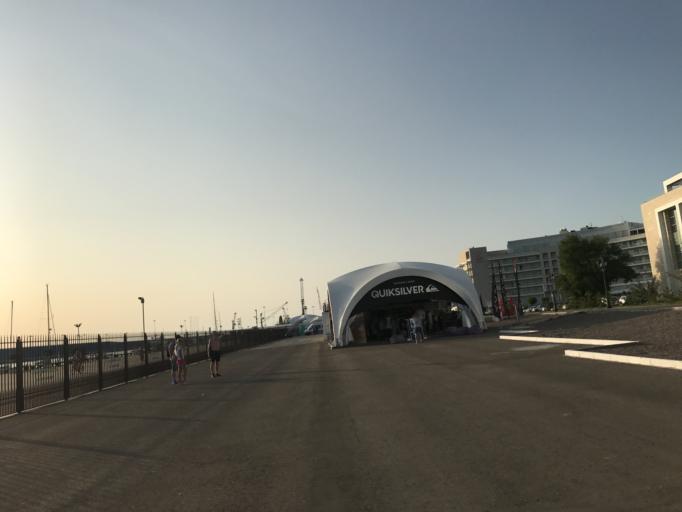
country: RU
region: Krasnodarskiy
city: Adler
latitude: 43.4094
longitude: 39.9372
